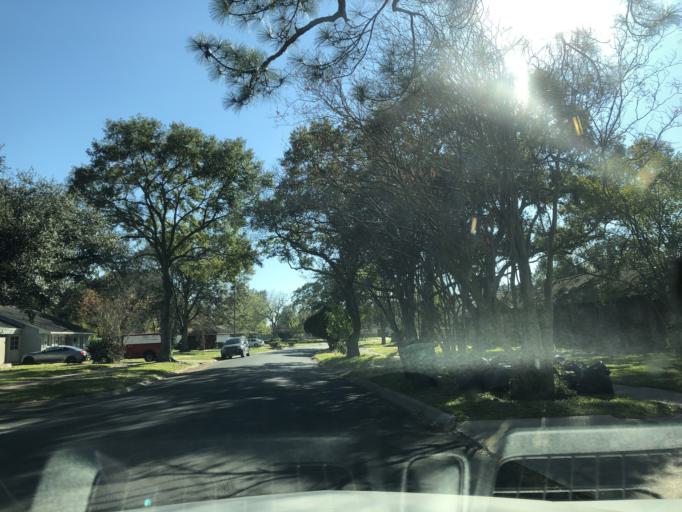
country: US
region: Texas
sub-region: Harris County
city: Bellaire
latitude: 29.6897
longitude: -95.5007
